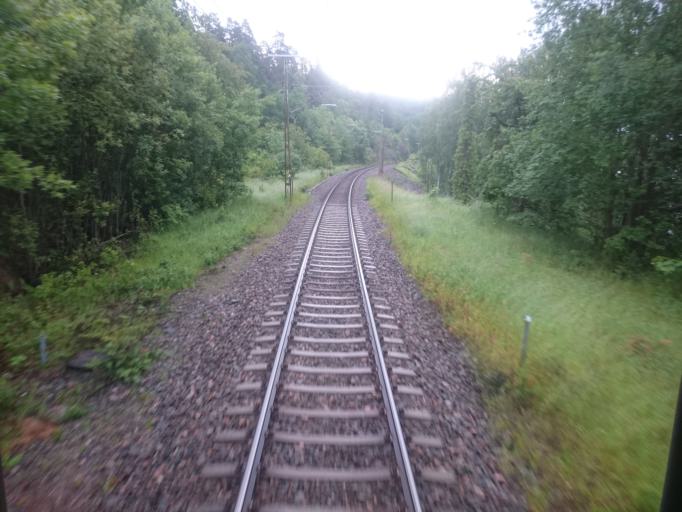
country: SE
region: OEstergoetland
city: Lindo
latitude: 58.6686
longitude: 16.2746
